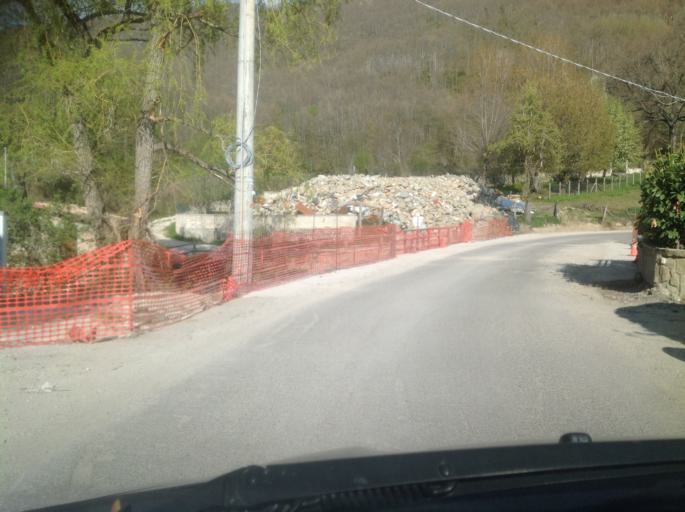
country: IT
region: Latium
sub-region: Provincia di Rieti
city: Amatrice
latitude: 42.6742
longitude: 13.2939
